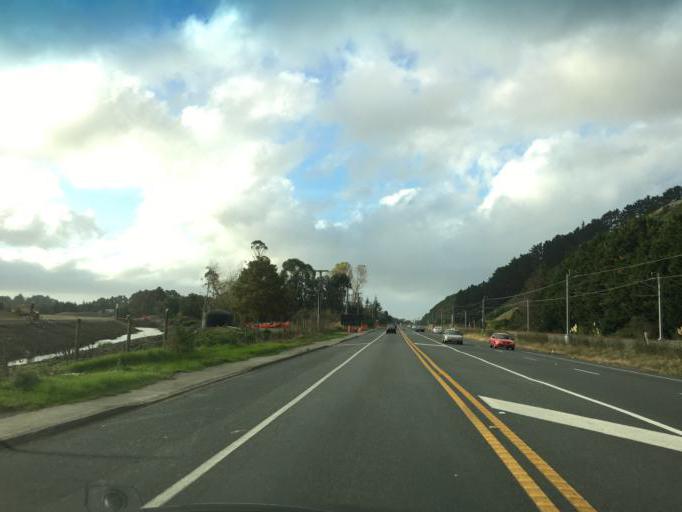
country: NZ
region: Wellington
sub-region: Kapiti Coast District
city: Paraparaumu
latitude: -40.9355
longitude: 174.9952
